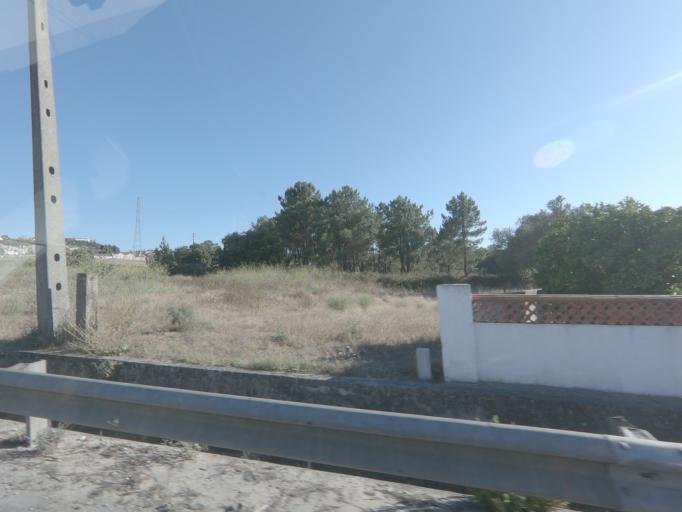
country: PT
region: Setubal
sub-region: Palmela
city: Palmela
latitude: 38.5821
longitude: -8.9104
